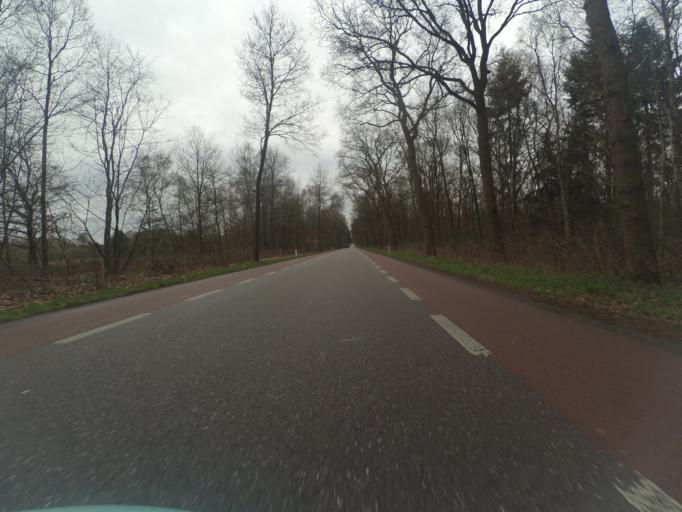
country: NL
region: Gelderland
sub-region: Gemeente Arnhem
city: Gulden Bodem
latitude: 52.0427
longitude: 5.9036
